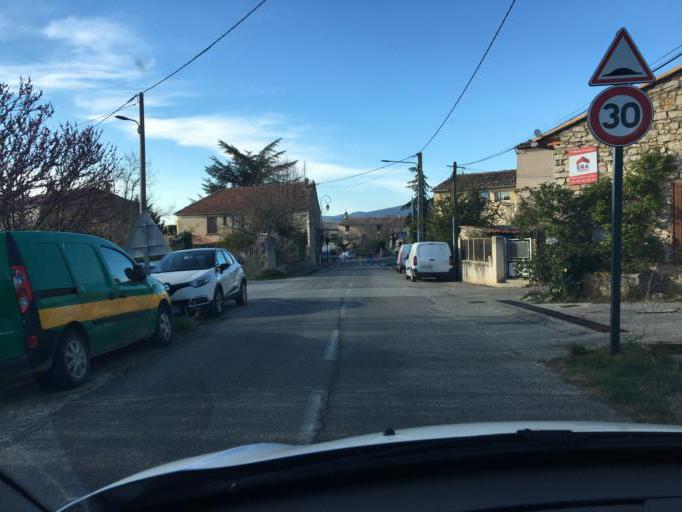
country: FR
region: Provence-Alpes-Cote d'Azur
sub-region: Departement du Vaucluse
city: Villes-sur-Auzon
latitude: 44.0560
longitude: 5.2371
